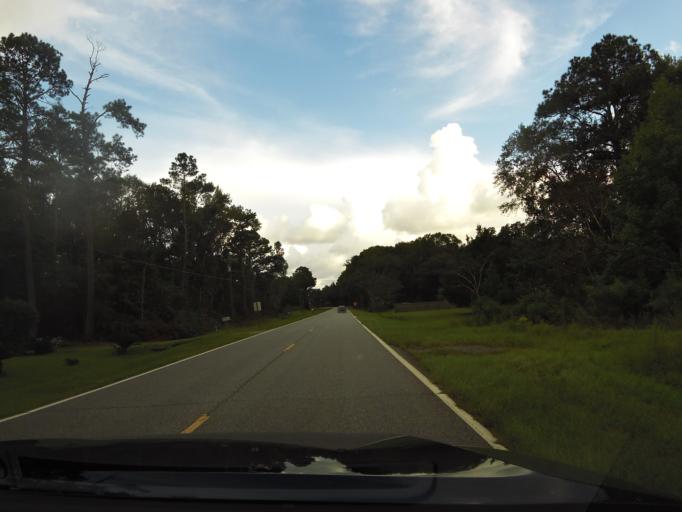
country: US
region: Georgia
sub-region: Liberty County
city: Midway
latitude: 31.8461
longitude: -81.4172
